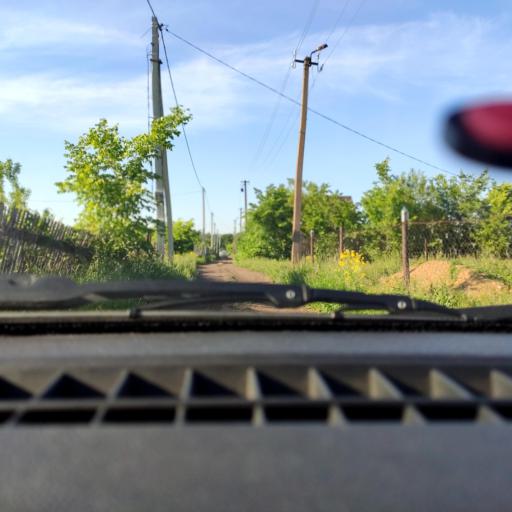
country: RU
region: Bashkortostan
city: Avdon
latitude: 54.4637
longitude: 55.8197
